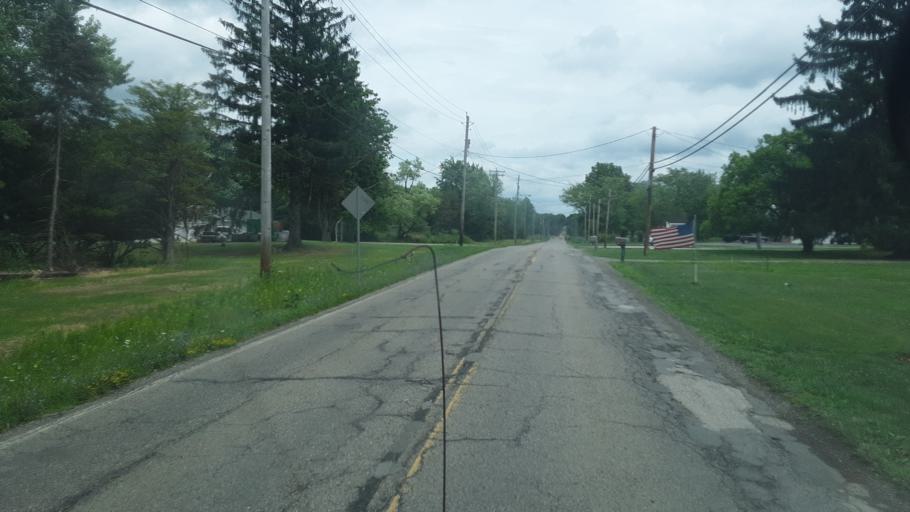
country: US
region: Ohio
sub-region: Trumbull County
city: Churchill
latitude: 41.1836
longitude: -80.6714
